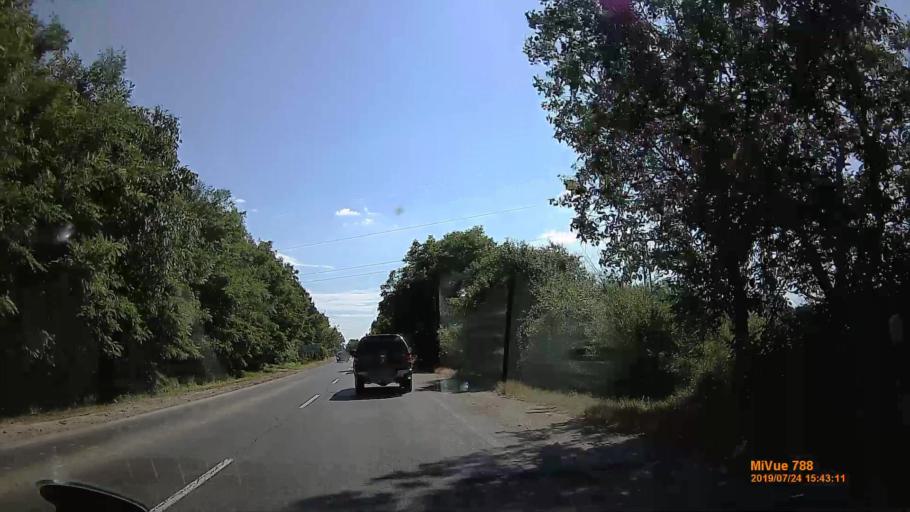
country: HU
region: Szabolcs-Szatmar-Bereg
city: Vasarosnameny
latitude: 48.1122
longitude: 22.3079
